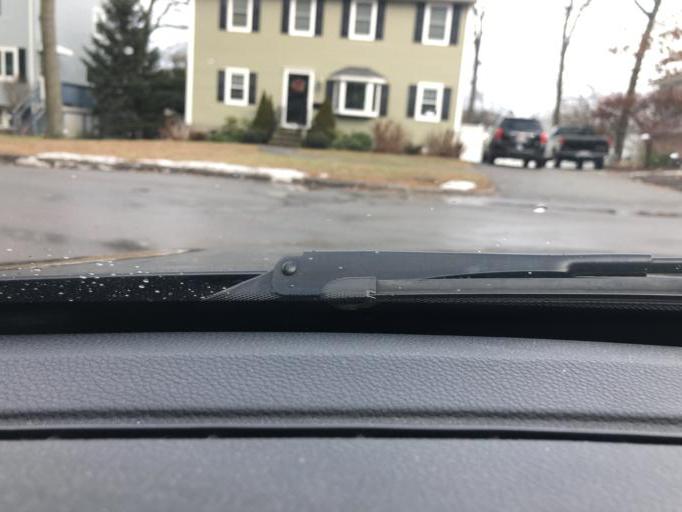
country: US
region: Massachusetts
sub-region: Middlesex County
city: Arlington
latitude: 42.4260
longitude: -71.1617
